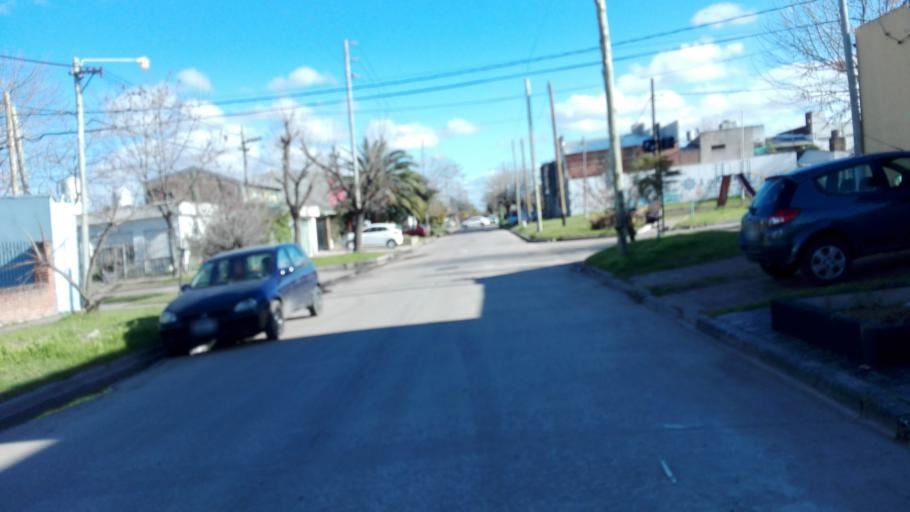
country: AR
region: Buenos Aires
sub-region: Partido de La Plata
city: La Plata
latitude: -34.8825
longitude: -57.9822
